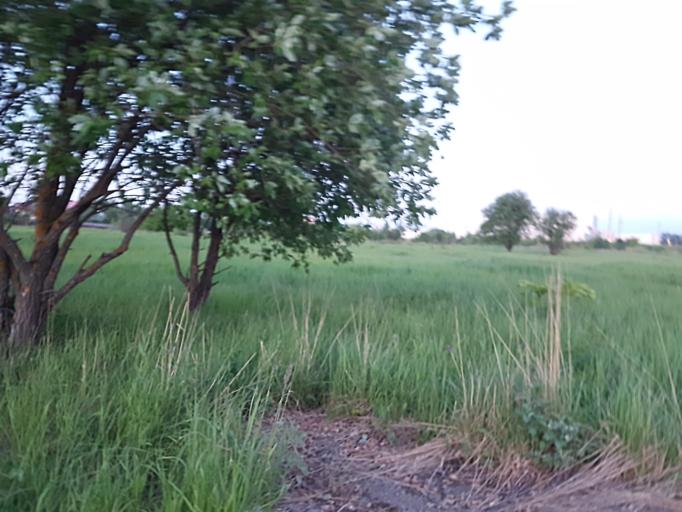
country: RU
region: Moskovskaya
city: Istra
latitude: 55.9055
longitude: 36.8769
